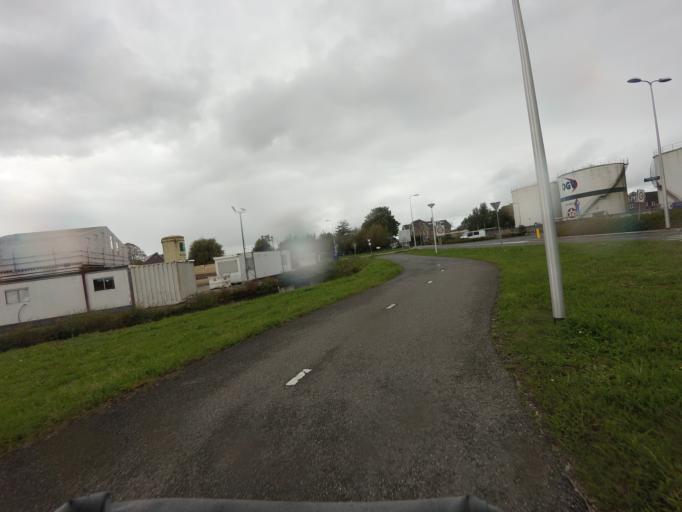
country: NL
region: South Holland
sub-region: Gemeente Alphen aan den Rijn
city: Alphen aan den Rijn
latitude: 52.1172
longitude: 4.6805
